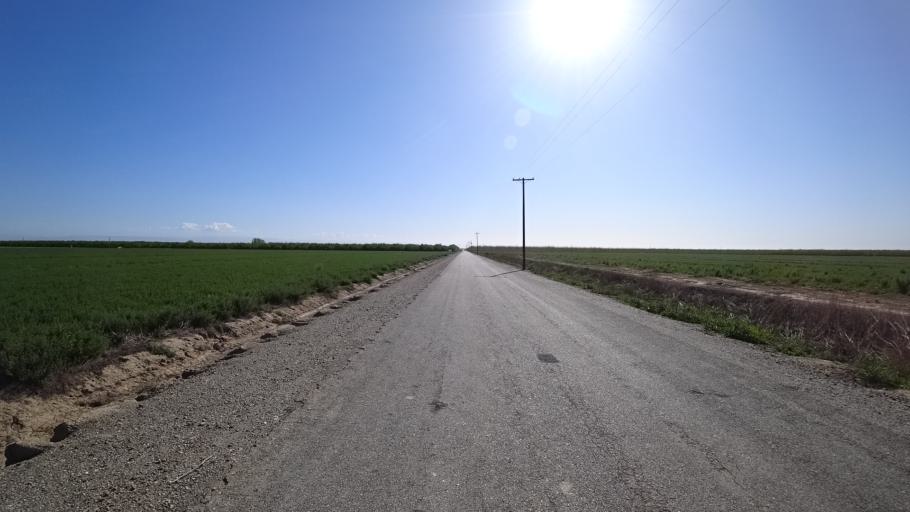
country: US
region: California
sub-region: Glenn County
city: Hamilton City
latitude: 39.6782
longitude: -122.0631
